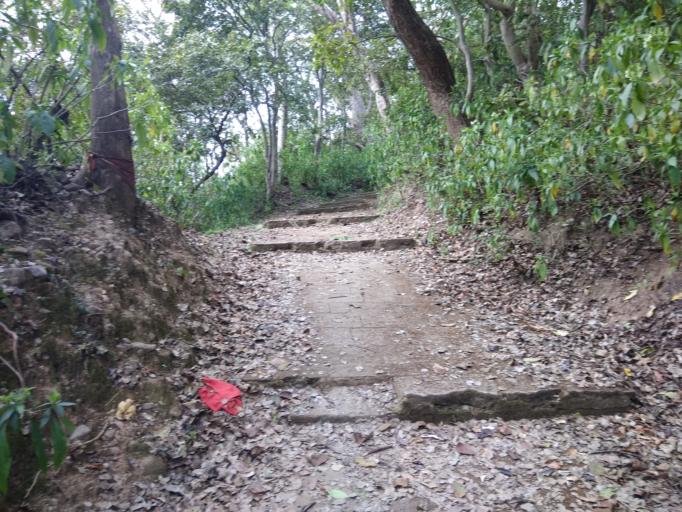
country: IN
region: Himachal Pradesh
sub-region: Kangra
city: Kotla
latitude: 32.2356
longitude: 76.0437
